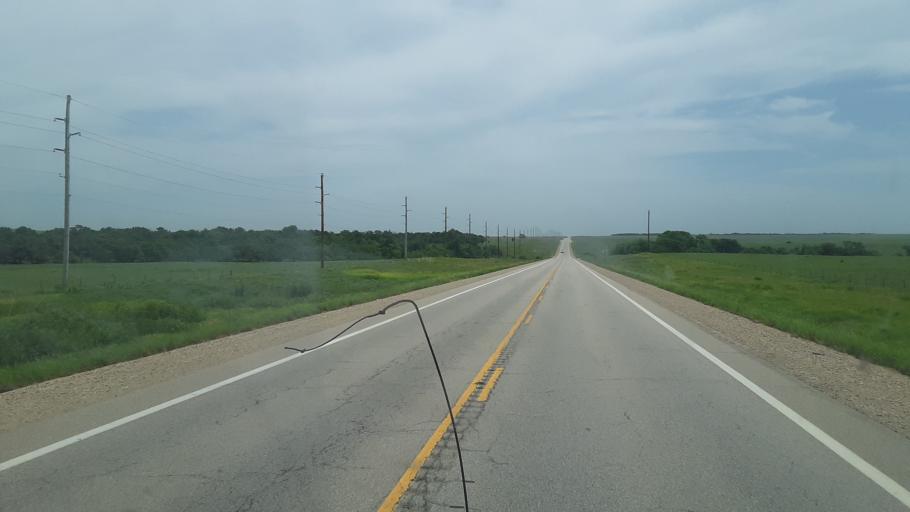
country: US
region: Kansas
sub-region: Greenwood County
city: Eureka
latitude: 37.8371
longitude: -96.0447
